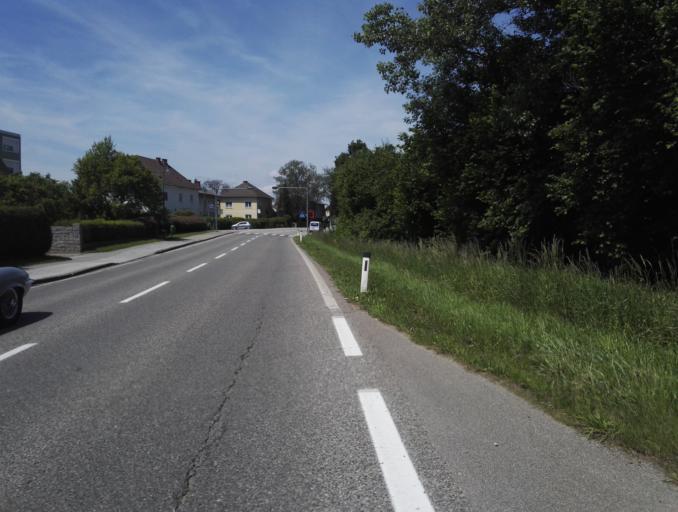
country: AT
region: Styria
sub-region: Politischer Bezirk Graz-Umgebung
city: Kalsdorf bei Graz
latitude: 46.9691
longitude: 15.4749
